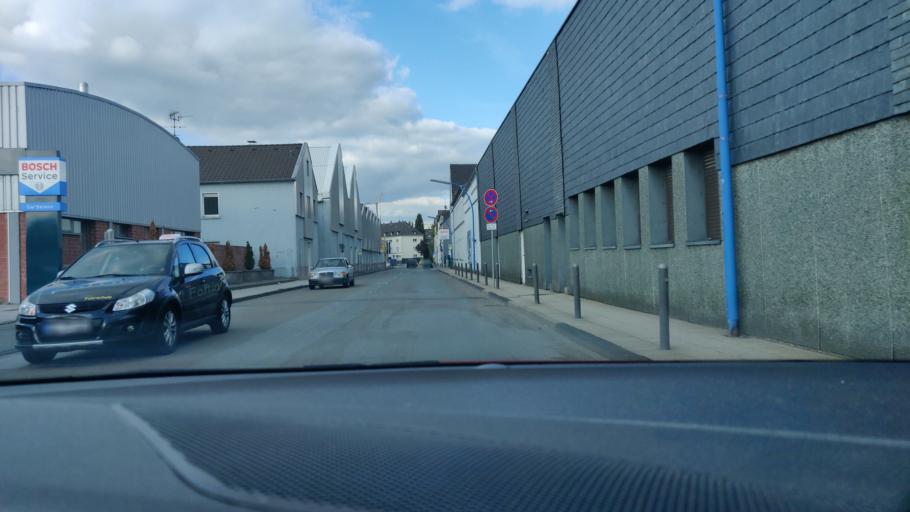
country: DE
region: North Rhine-Westphalia
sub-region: Regierungsbezirk Dusseldorf
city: Velbert
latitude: 51.3278
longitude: 7.0489
